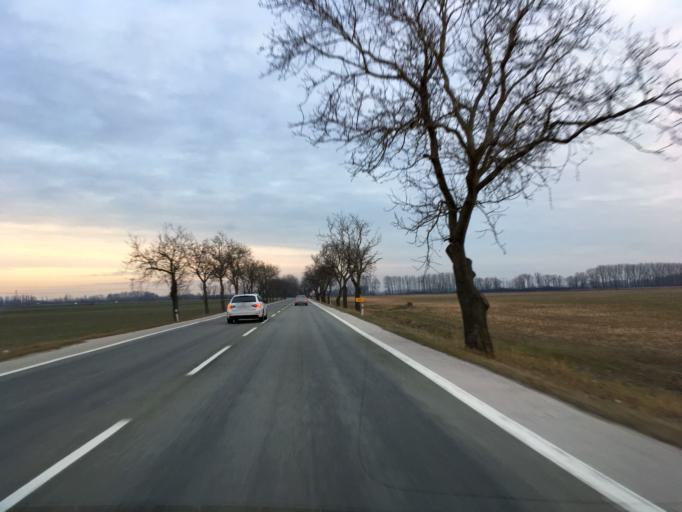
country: SK
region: Trnavsky
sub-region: Okres Dunajska Streda
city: Velky Meder
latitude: 47.8934
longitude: 17.7417
